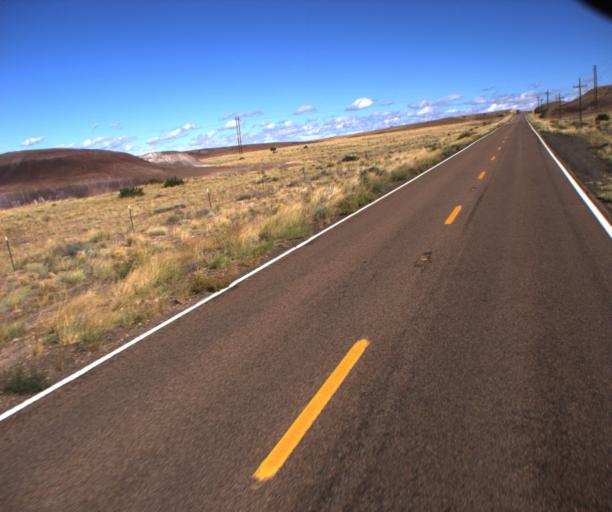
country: US
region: Arizona
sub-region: Apache County
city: Saint Johns
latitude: 34.5532
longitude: -109.3430
